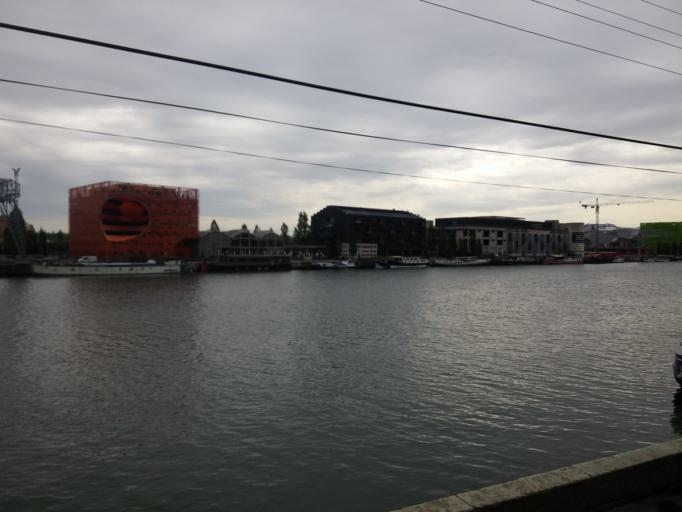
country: FR
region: Rhone-Alpes
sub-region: Departement du Rhone
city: La Mulatiere
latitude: 45.7397
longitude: 4.8121
